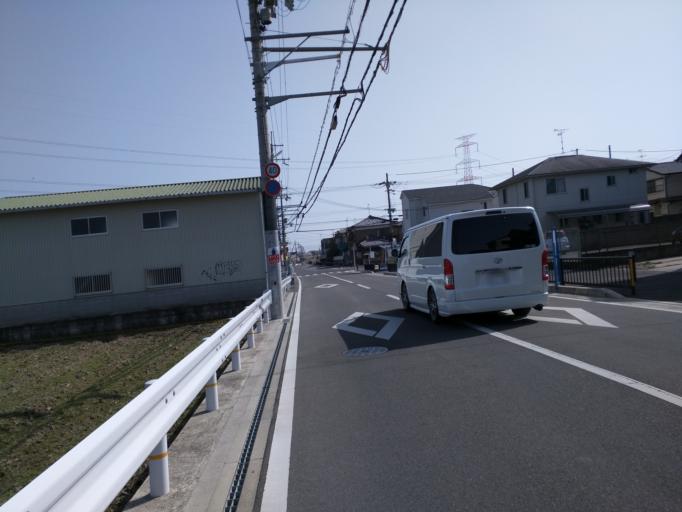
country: JP
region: Kyoto
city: Tanabe
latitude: 34.7596
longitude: 135.7973
